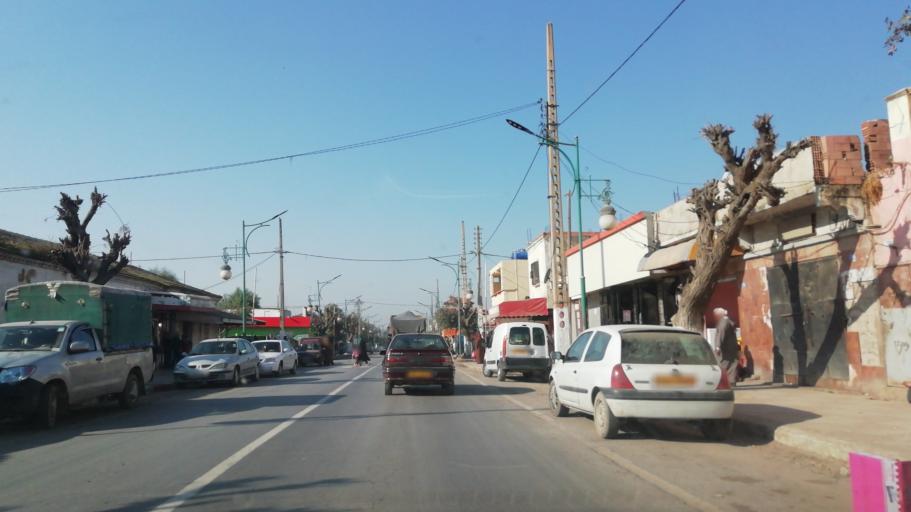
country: DZ
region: Relizane
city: Relizane
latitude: 35.7338
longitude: 0.4605
